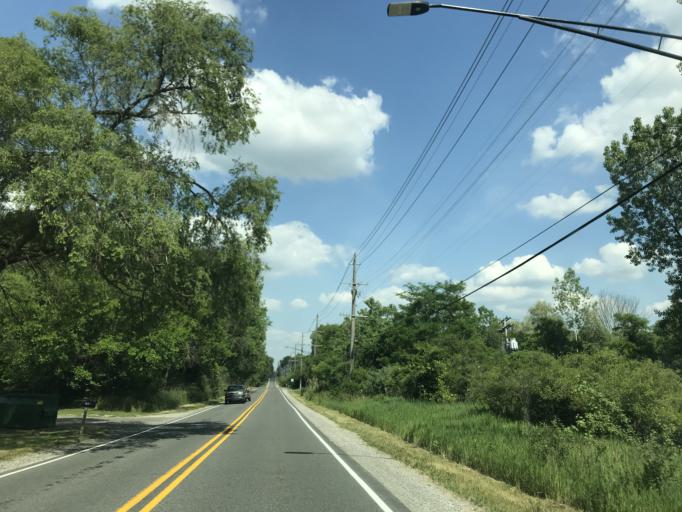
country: US
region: Michigan
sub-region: Washtenaw County
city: Ypsilanti
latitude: 42.2605
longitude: -83.6187
